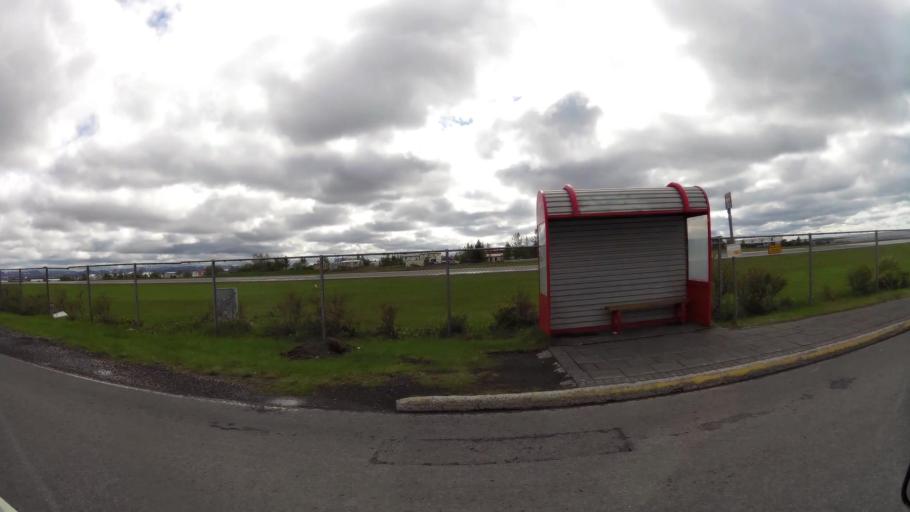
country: IS
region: Capital Region
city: Kopavogur
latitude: 64.1328
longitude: -21.9526
